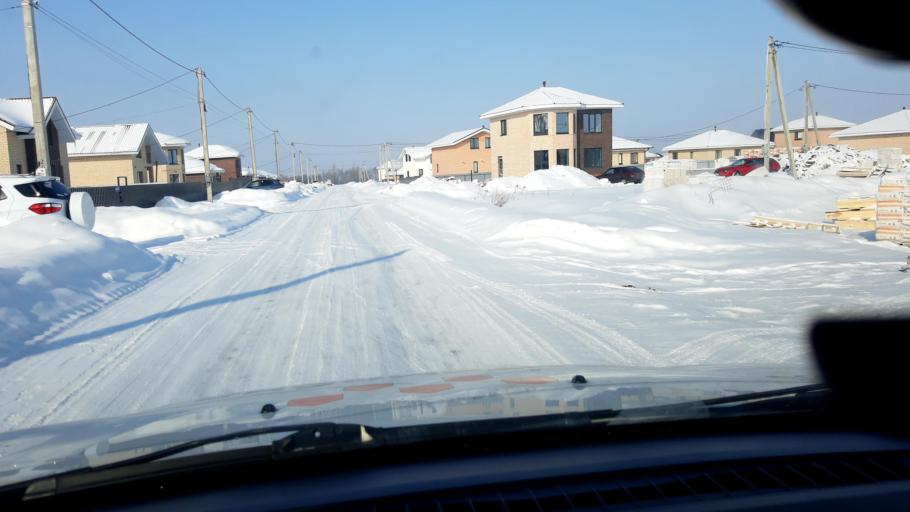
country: RU
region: Bashkortostan
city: Kabakovo
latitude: 54.6381
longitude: 56.1087
